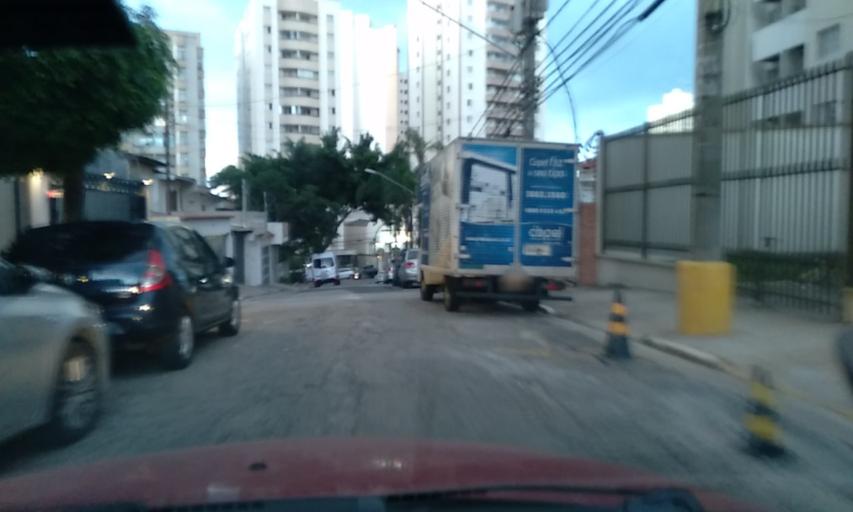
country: BR
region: Sao Paulo
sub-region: Sao Paulo
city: Sao Paulo
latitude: -23.6078
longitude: -46.6213
